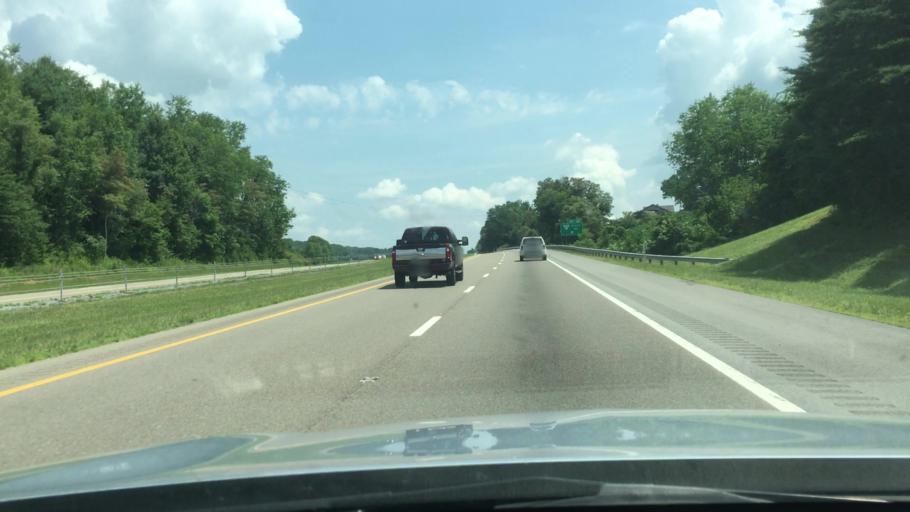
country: US
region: Tennessee
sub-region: Unicoi County
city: Unicoi
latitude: 36.2021
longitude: -82.3587
